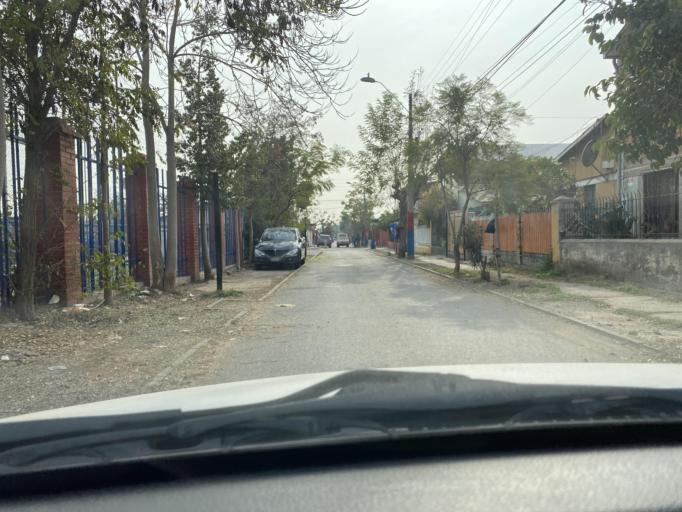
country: CL
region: Santiago Metropolitan
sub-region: Provincia de Santiago
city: La Pintana
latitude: -33.5194
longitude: -70.6258
